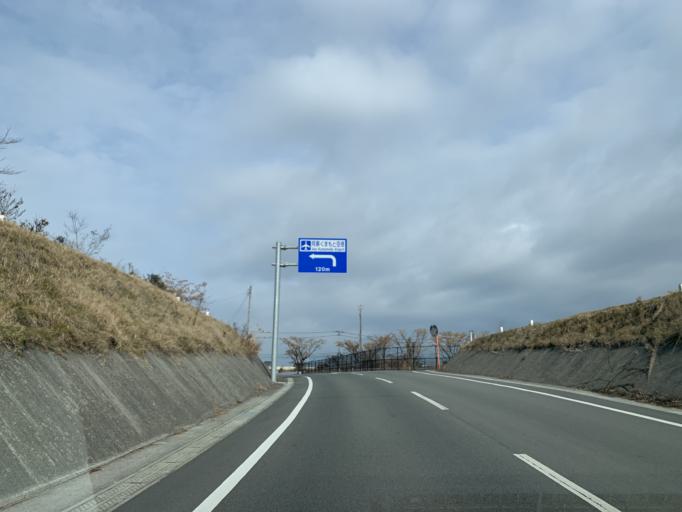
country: JP
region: Kumamoto
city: Ozu
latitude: 32.8330
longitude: 130.8630
